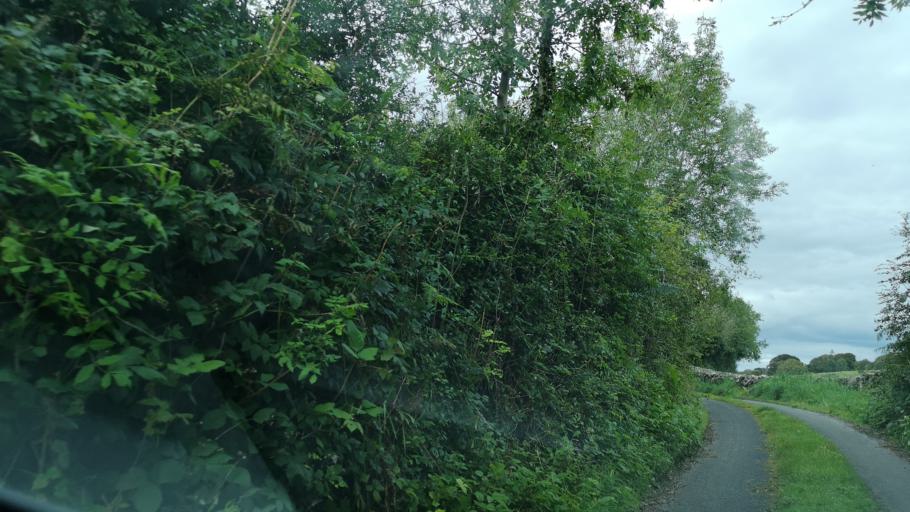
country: IE
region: Connaught
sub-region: County Galway
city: Loughrea
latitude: 53.1599
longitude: -8.4541
